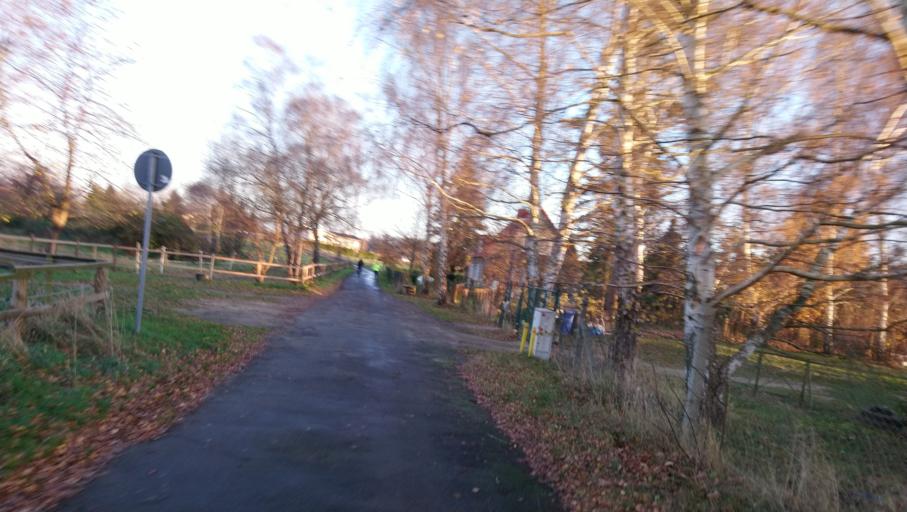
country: DE
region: Mecklenburg-Vorpommern
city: Kritzmow
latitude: 54.0654
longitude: 12.0973
